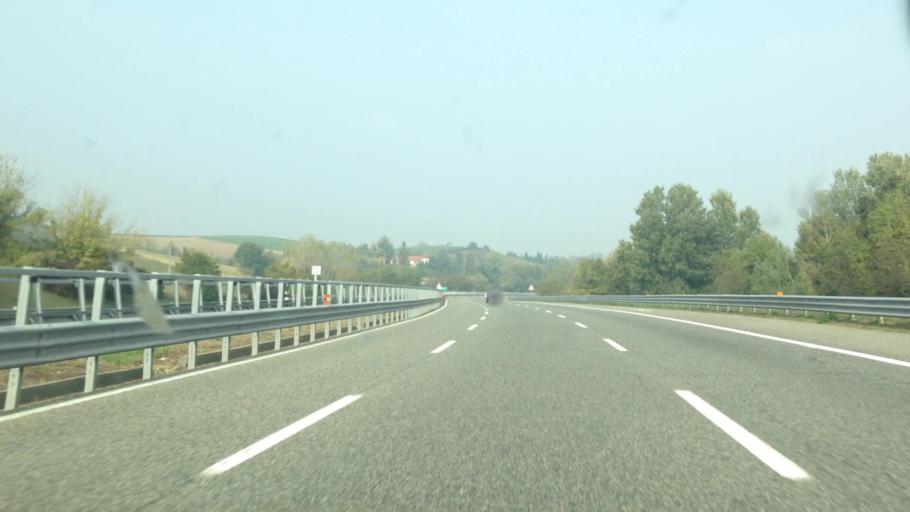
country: IT
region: Piedmont
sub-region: Provincia di Alessandria
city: San Salvatore Monferrato
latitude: 45.0017
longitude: 8.5392
